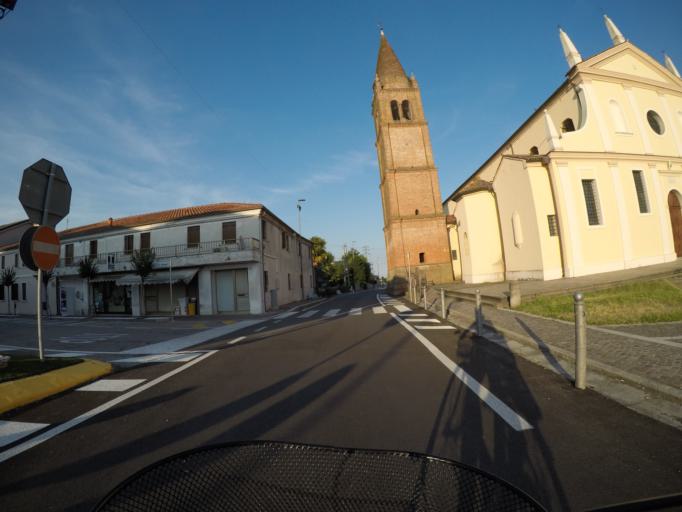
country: IT
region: Veneto
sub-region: Provincia di Rovigo
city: San Bellino
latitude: 45.0279
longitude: 11.5891
